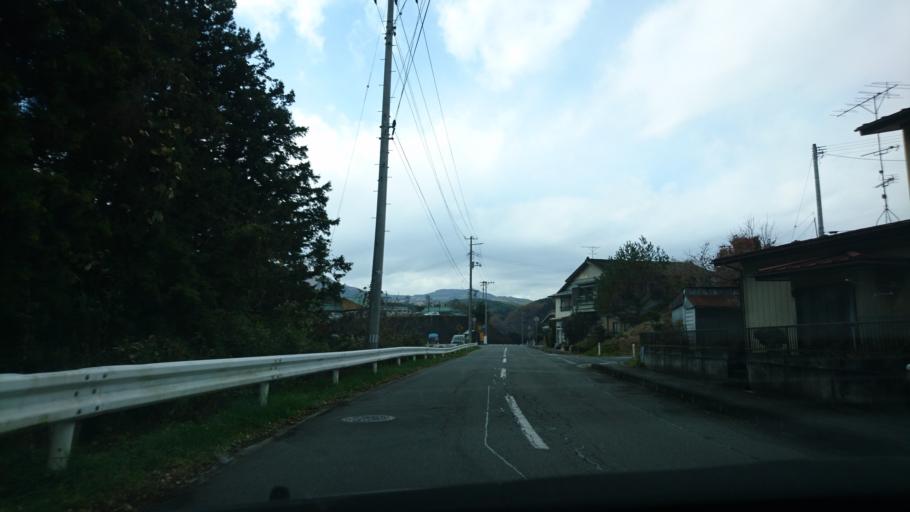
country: JP
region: Iwate
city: Ichinoseki
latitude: 38.9941
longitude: 141.2497
